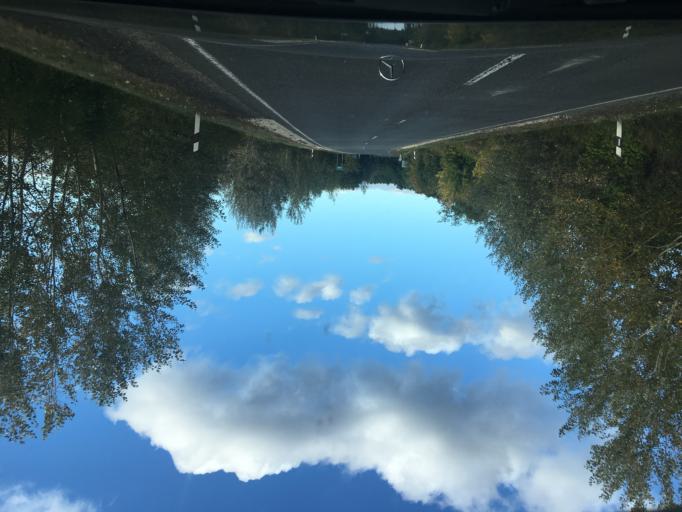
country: HU
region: Borsod-Abauj-Zemplen
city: Encs
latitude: 48.4282
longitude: 21.1814
